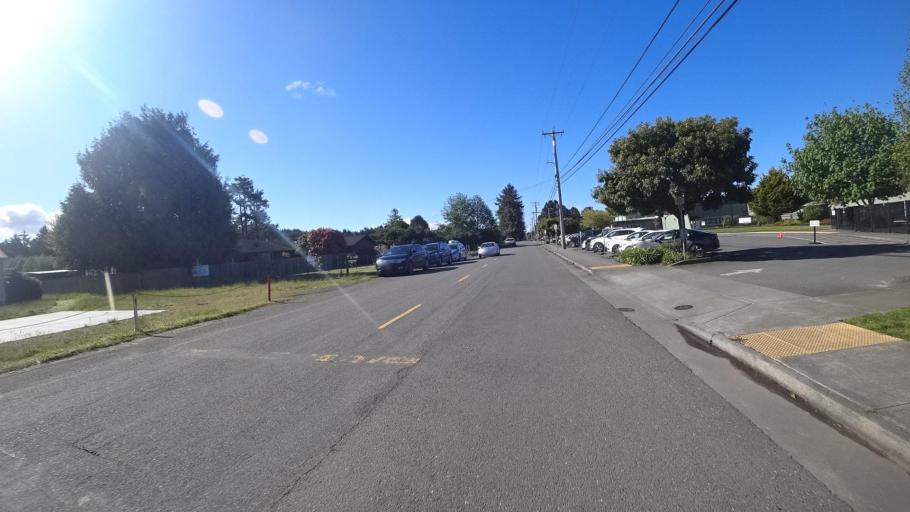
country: US
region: California
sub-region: Humboldt County
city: McKinleyville
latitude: 40.9777
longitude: -124.0959
